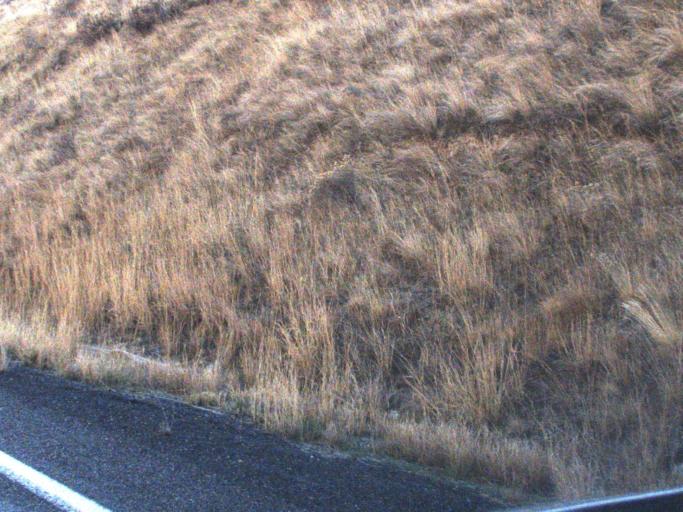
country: US
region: Washington
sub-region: Garfield County
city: Pomeroy
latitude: 46.4372
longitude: -117.3600
